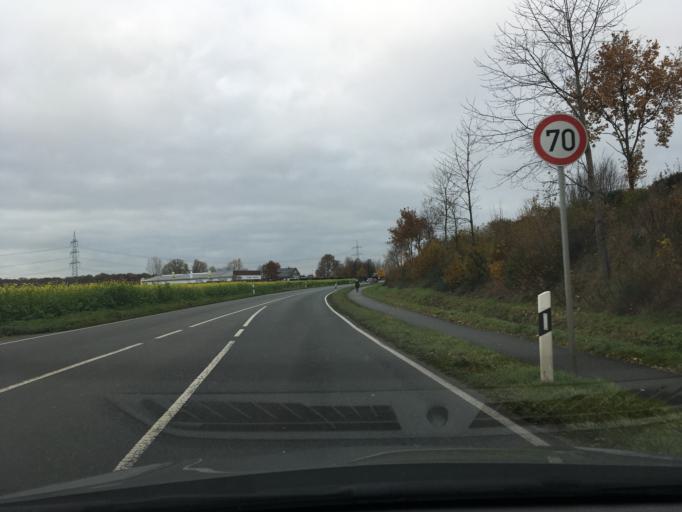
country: DE
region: North Rhine-Westphalia
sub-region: Regierungsbezirk Munster
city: Ahaus
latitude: 52.0858
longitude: 6.9670
